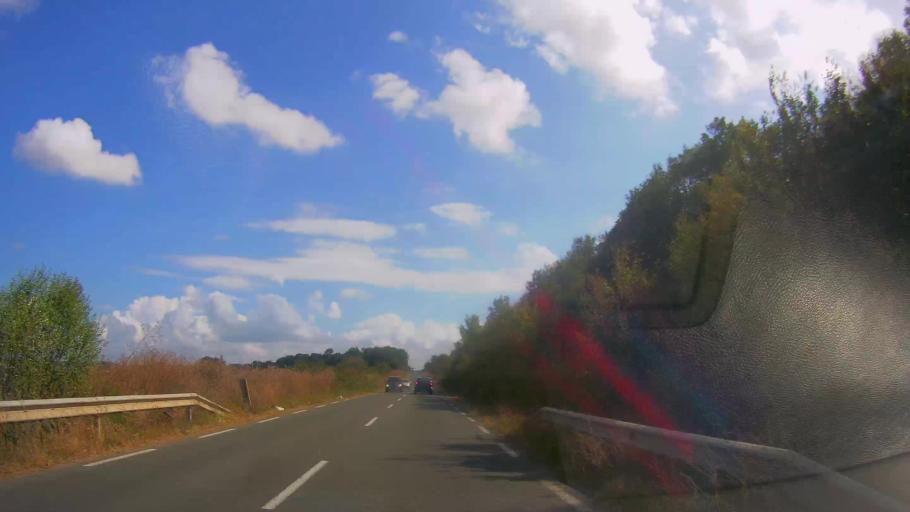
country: BG
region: Burgas
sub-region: Obshtina Kameno
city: Kameno
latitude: 42.4852
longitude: 27.3423
